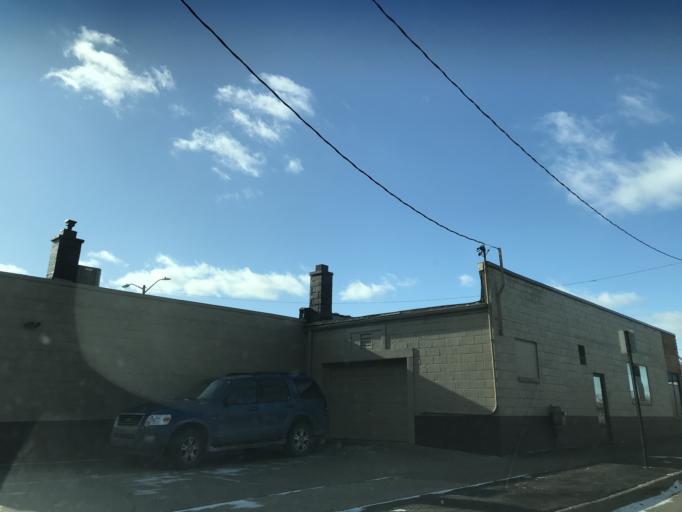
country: US
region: Michigan
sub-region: Oakland County
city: Hazel Park
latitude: 42.4570
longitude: -83.0959
